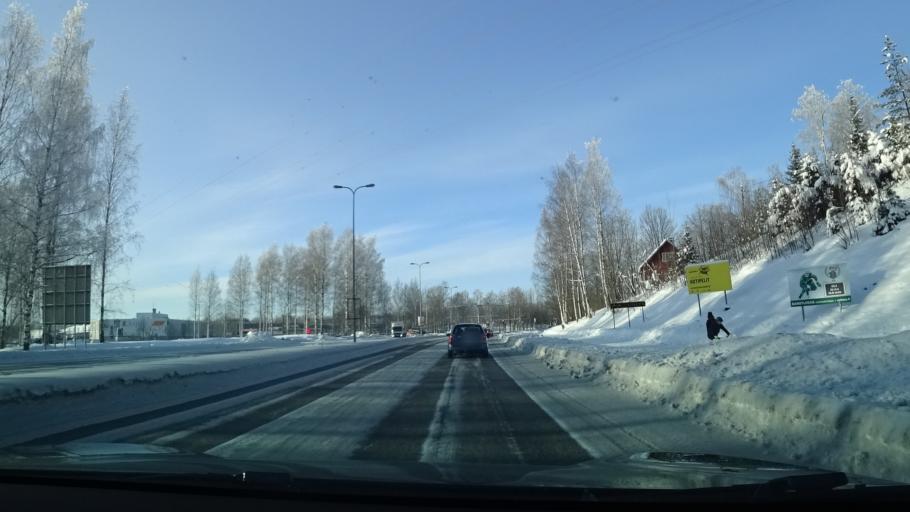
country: FI
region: South Karelia
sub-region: Lappeenranta
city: Lappeenranta
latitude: 61.0460
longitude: 28.2041
